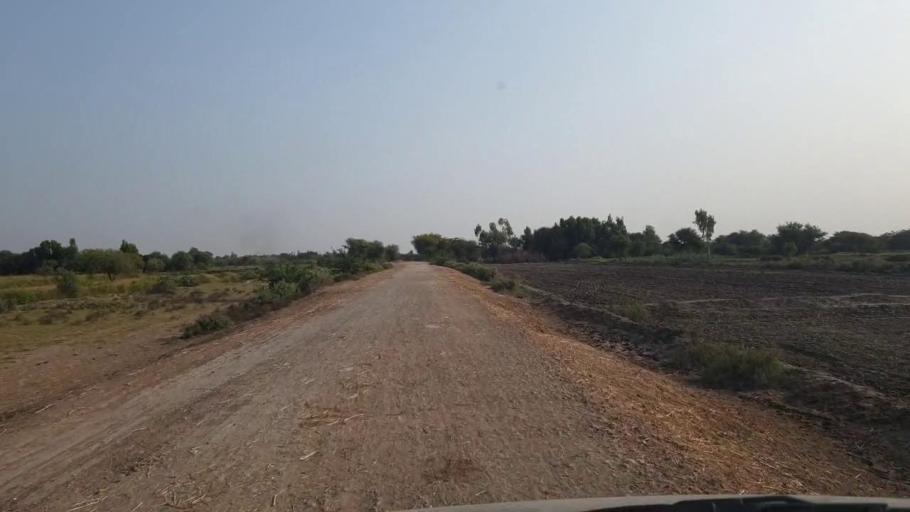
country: PK
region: Sindh
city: Rajo Khanani
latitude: 25.0401
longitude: 68.7686
